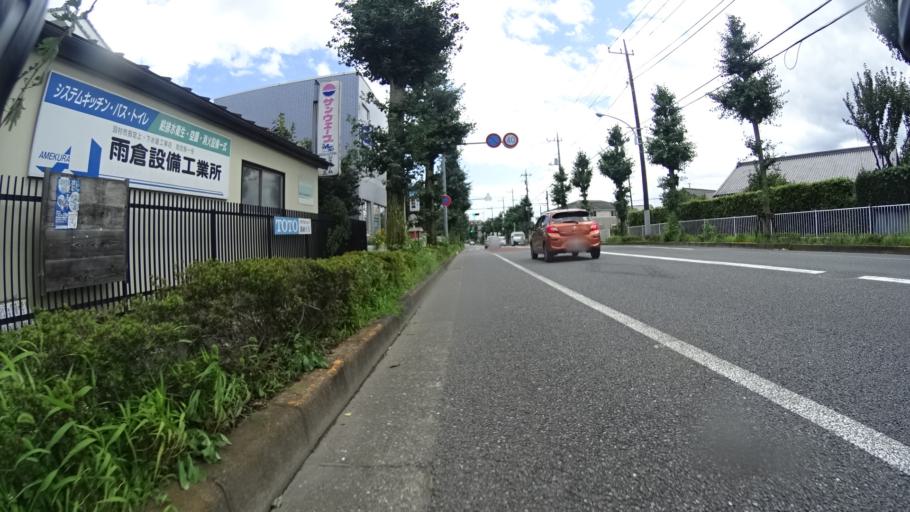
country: JP
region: Tokyo
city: Fussa
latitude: 35.7525
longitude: 139.3175
